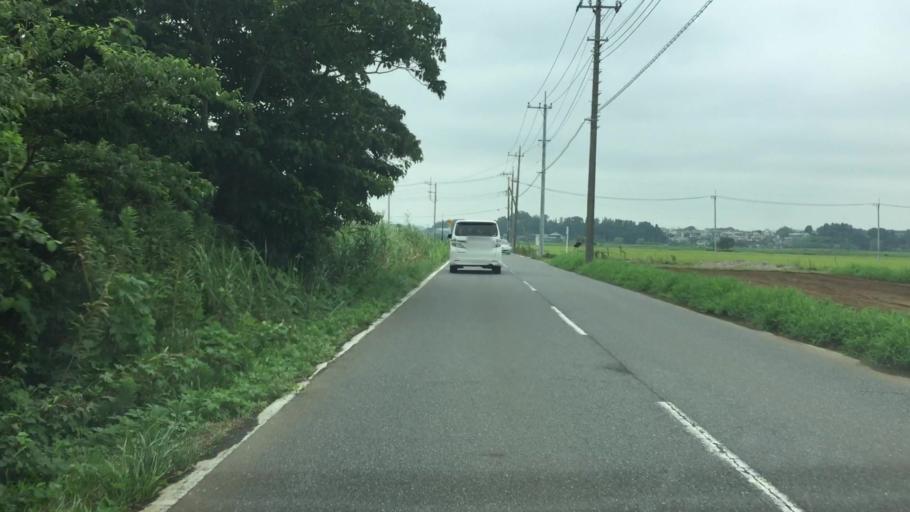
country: JP
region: Chiba
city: Abiko
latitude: 35.8534
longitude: 140.0438
